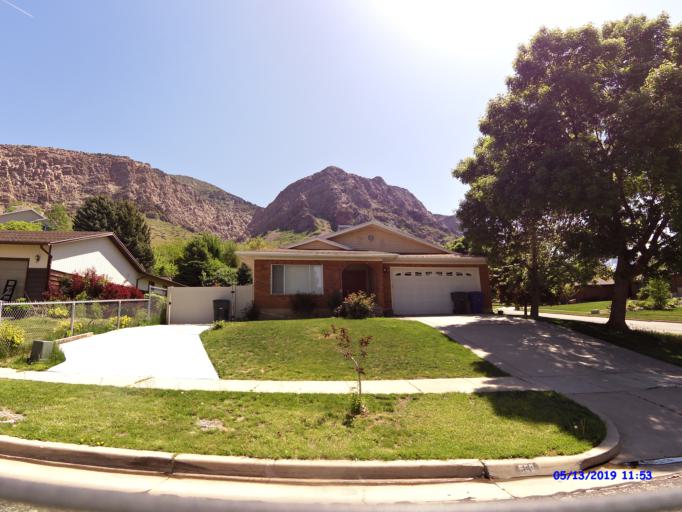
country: US
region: Utah
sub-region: Weber County
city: North Ogden
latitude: 41.2700
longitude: -111.9505
